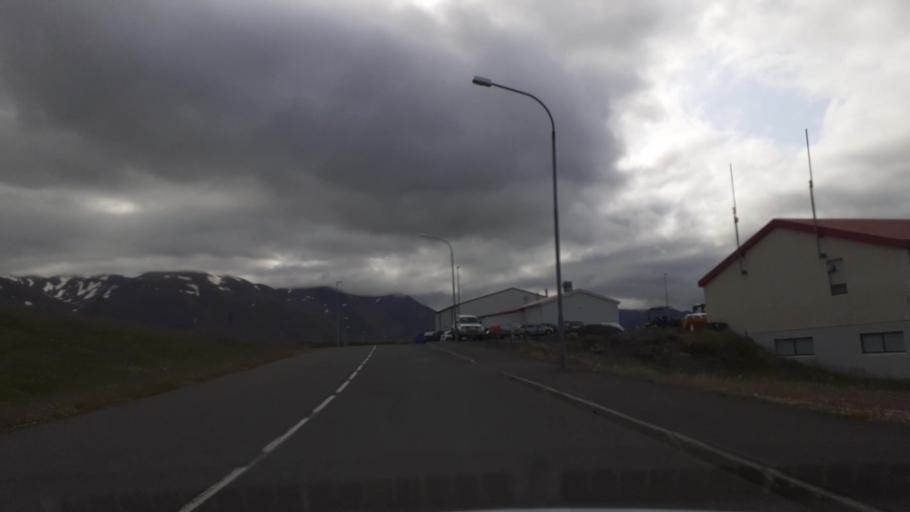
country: IS
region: Northeast
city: Akureyri
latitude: 65.9528
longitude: -18.1793
